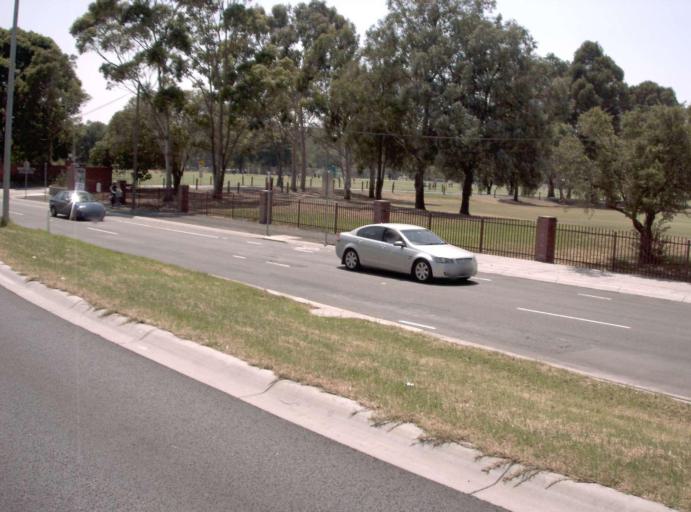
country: AU
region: Victoria
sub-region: Manningham
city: Bulleen
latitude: -37.7756
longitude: 145.0786
